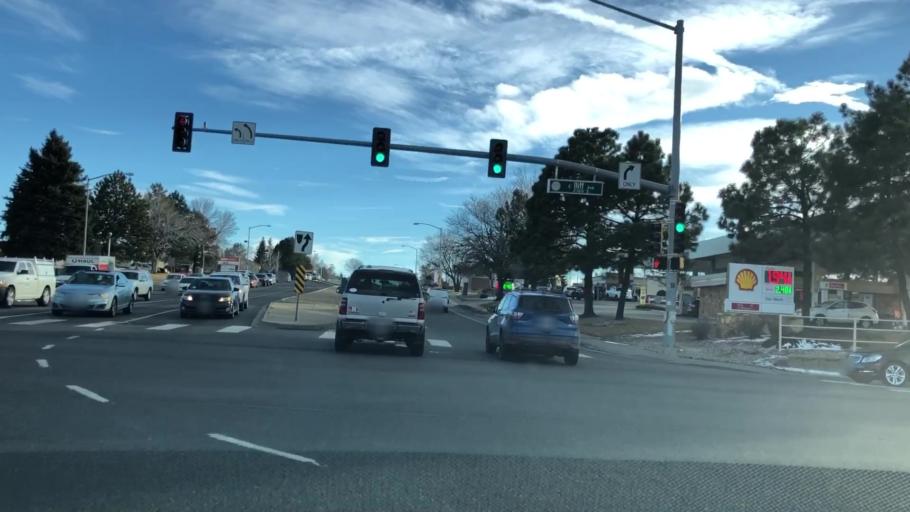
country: US
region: Colorado
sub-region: Adams County
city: Aurora
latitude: 39.6739
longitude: -104.7912
